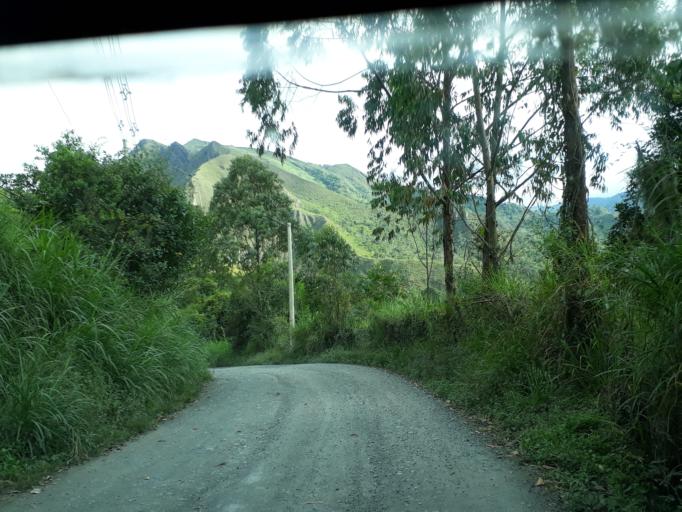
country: CO
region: Cundinamarca
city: Pacho
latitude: 5.1862
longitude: -74.1937
